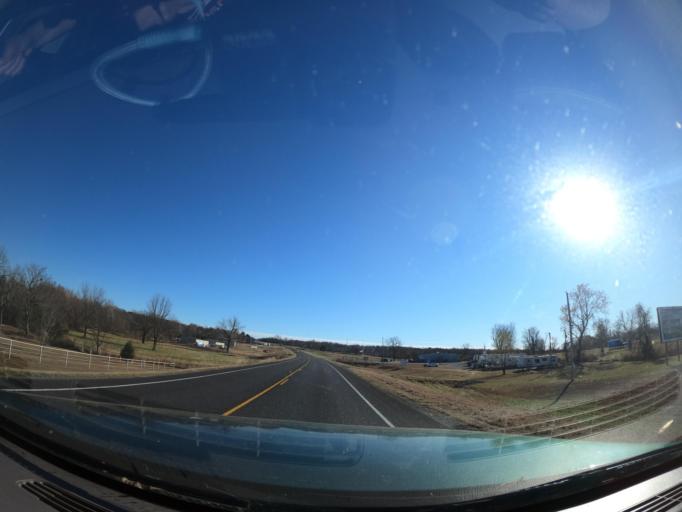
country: US
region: Oklahoma
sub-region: McIntosh County
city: Eufaula
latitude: 35.2592
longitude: -95.5788
